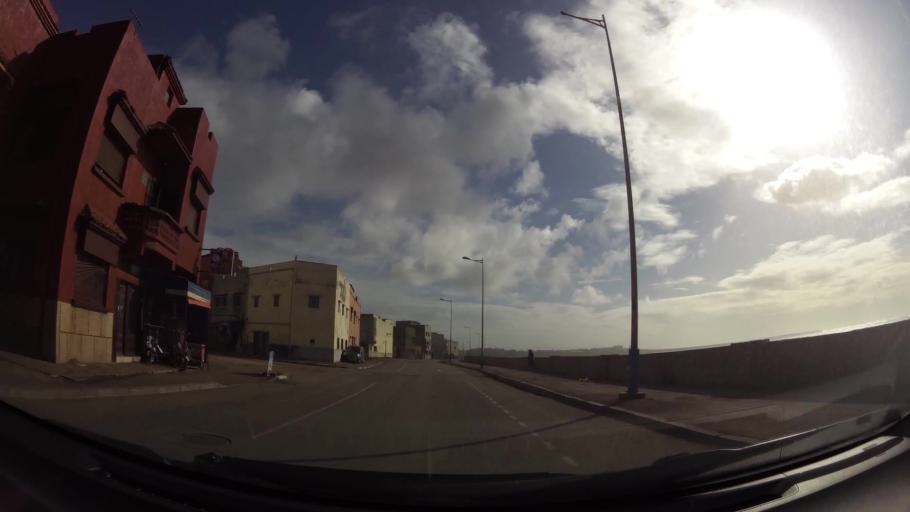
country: MA
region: Doukkala-Abda
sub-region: El-Jadida
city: El Jadida
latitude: 33.2610
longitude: -8.5146
